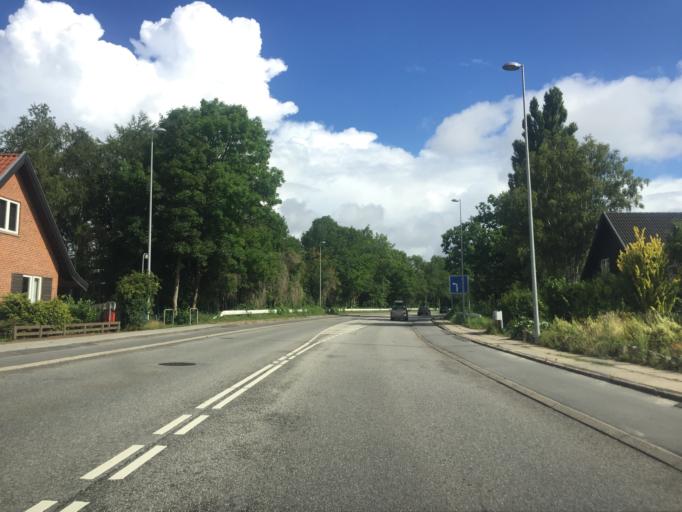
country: DK
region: South Denmark
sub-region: Odense Kommune
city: Odense
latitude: 55.3609
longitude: 10.3837
